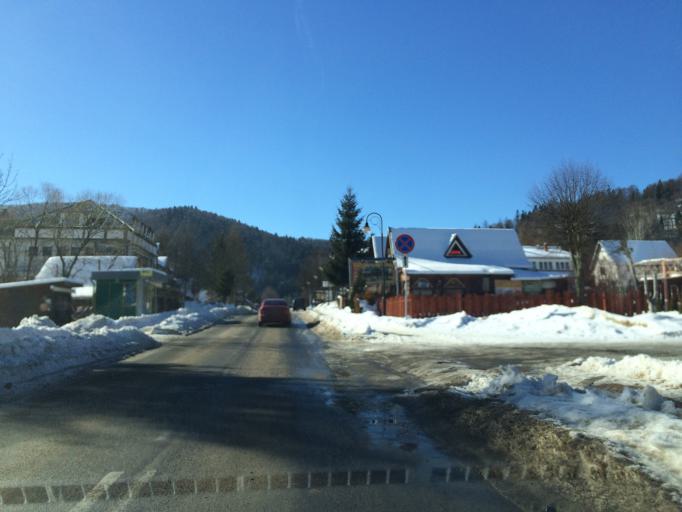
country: PL
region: Subcarpathian Voivodeship
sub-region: Powiat leski
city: Cisna
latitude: 49.2108
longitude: 22.3289
